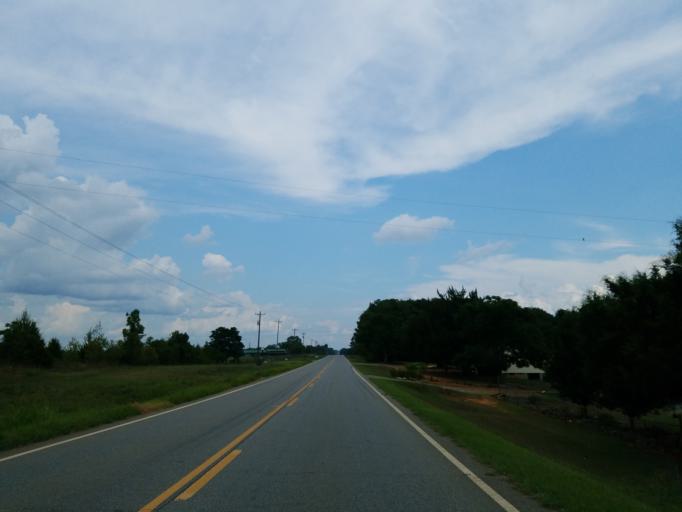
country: US
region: Georgia
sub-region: Dooly County
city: Unadilla
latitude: 32.3338
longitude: -83.7569
